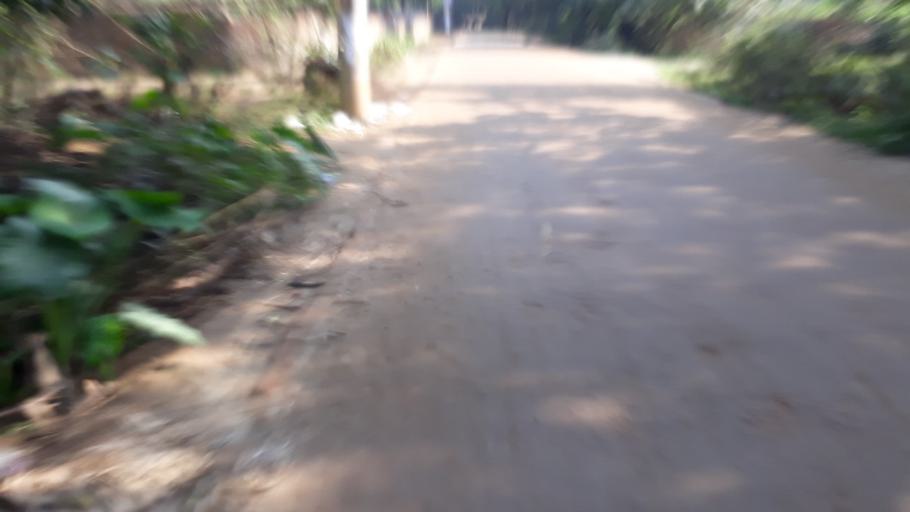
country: BD
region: Dhaka
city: Tungi
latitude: 23.8545
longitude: 90.3010
